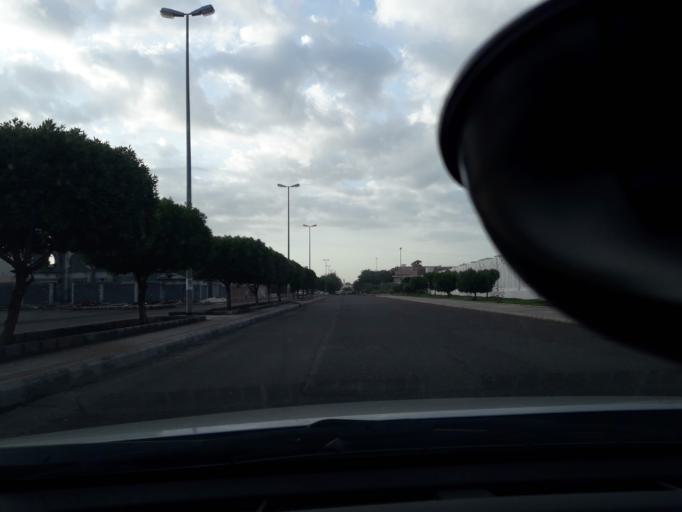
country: SA
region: Al Madinah al Munawwarah
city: Medina
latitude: 24.4255
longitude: 39.6269
